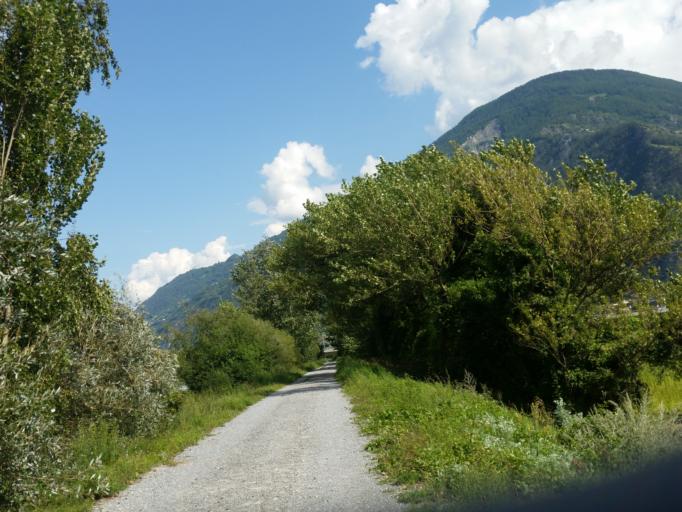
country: CH
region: Valais
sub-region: Martigny District
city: Leytron
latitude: 46.1776
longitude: 7.2113
